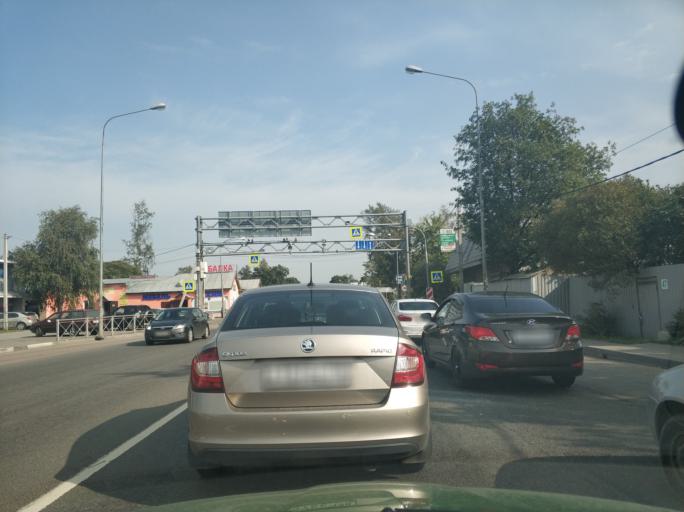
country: RU
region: Leningrad
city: Murino
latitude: 60.0432
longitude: 30.4453
